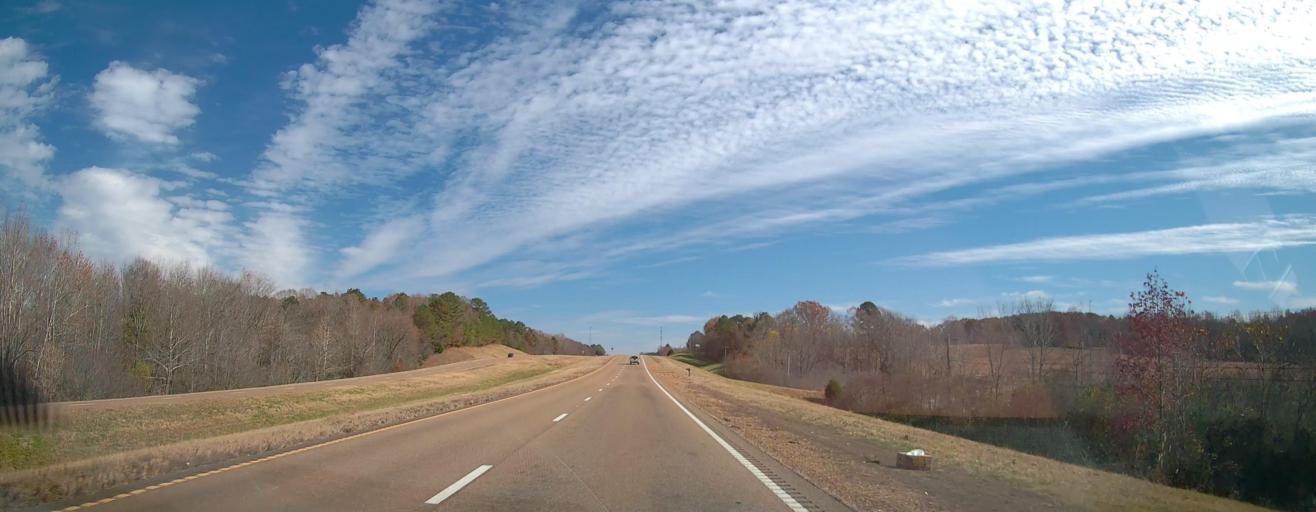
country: US
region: Mississippi
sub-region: Benton County
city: Ashland
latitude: 34.9457
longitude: -89.1639
